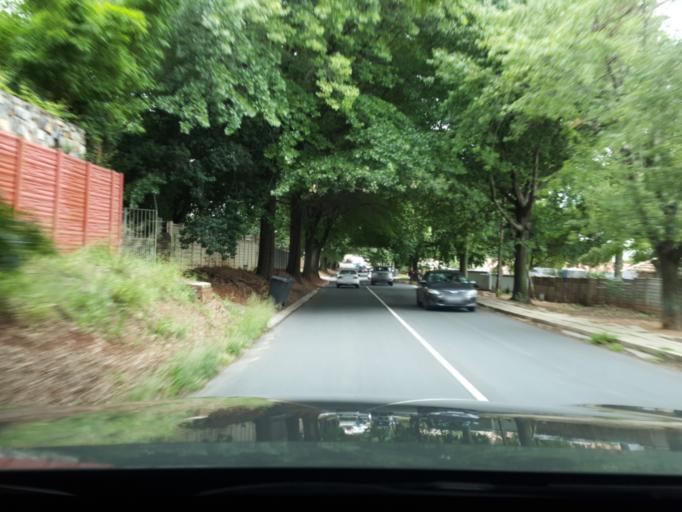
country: ZA
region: Gauteng
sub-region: City of Johannesburg Metropolitan Municipality
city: Johannesburg
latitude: -26.1195
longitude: 28.0051
